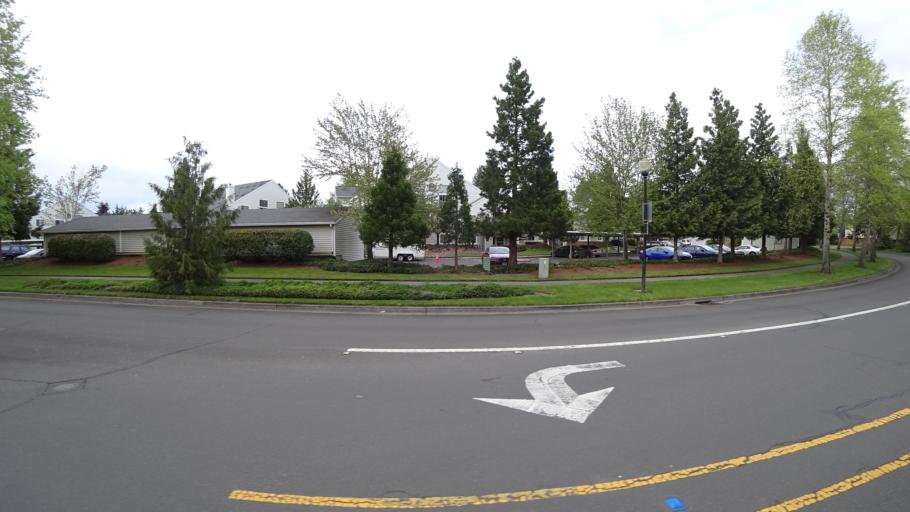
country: US
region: Oregon
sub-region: Washington County
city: Hillsboro
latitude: 45.5427
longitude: -122.9697
